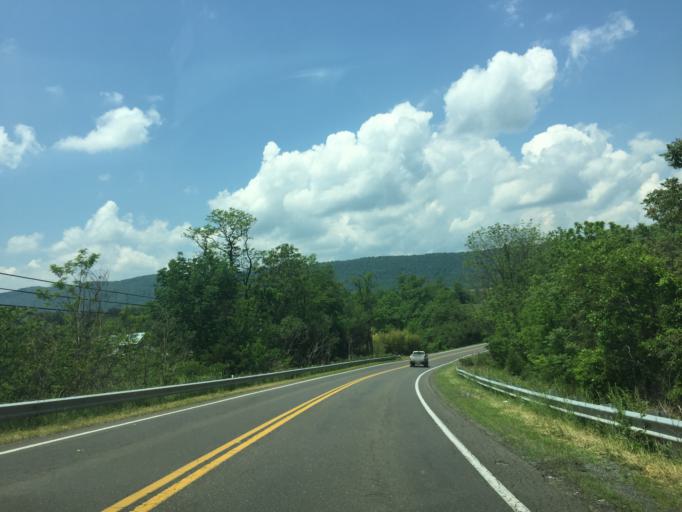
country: US
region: Virginia
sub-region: Shenandoah County
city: Strasburg
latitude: 39.0340
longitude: -78.3806
